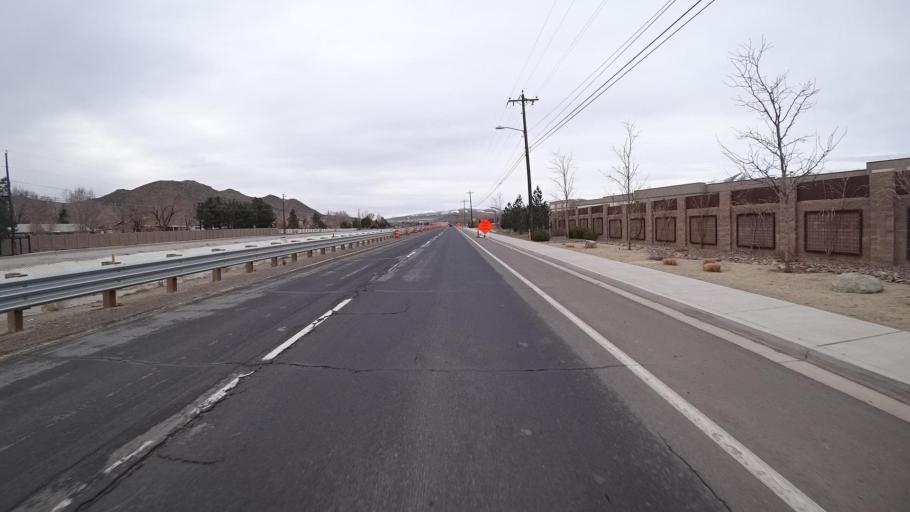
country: US
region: Nevada
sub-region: Washoe County
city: Lemmon Valley
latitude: 39.6314
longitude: -119.8457
